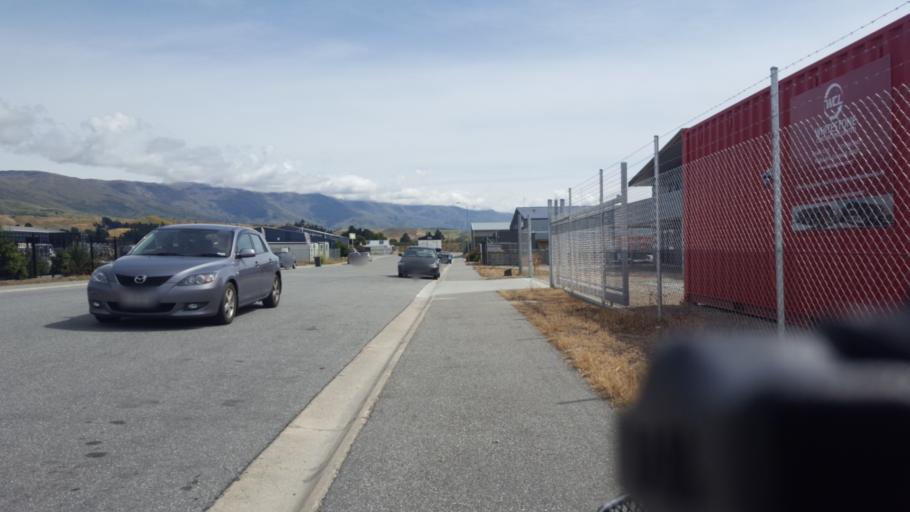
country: NZ
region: Otago
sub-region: Queenstown-Lakes District
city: Wanaka
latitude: -45.0513
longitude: 169.1916
